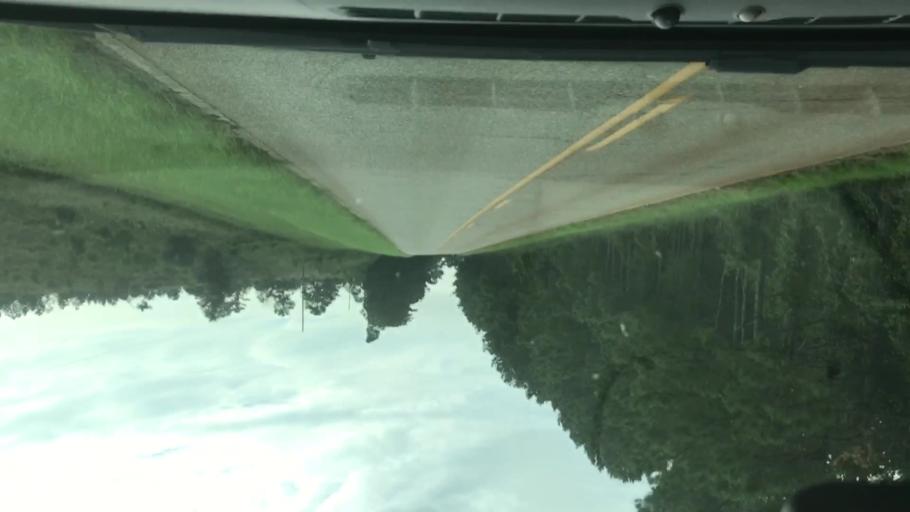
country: US
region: Georgia
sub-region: Quitman County
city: Georgetown
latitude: 31.9229
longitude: -85.0206
